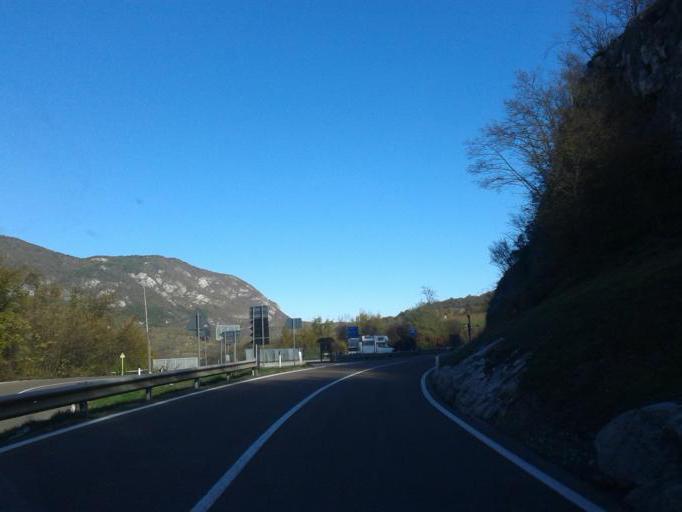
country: IT
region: Trentino-Alto Adige
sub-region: Provincia di Trento
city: Terlago
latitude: 46.0910
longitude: 11.0543
